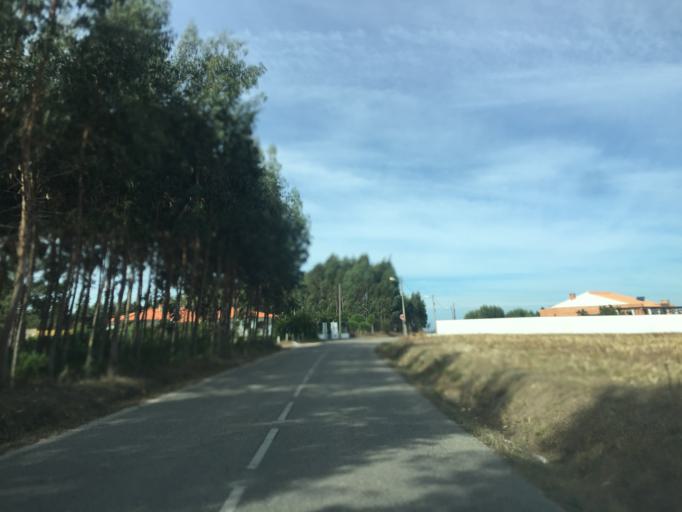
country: PT
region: Coimbra
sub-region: Figueira da Foz
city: Lavos
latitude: 40.0789
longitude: -8.8261
